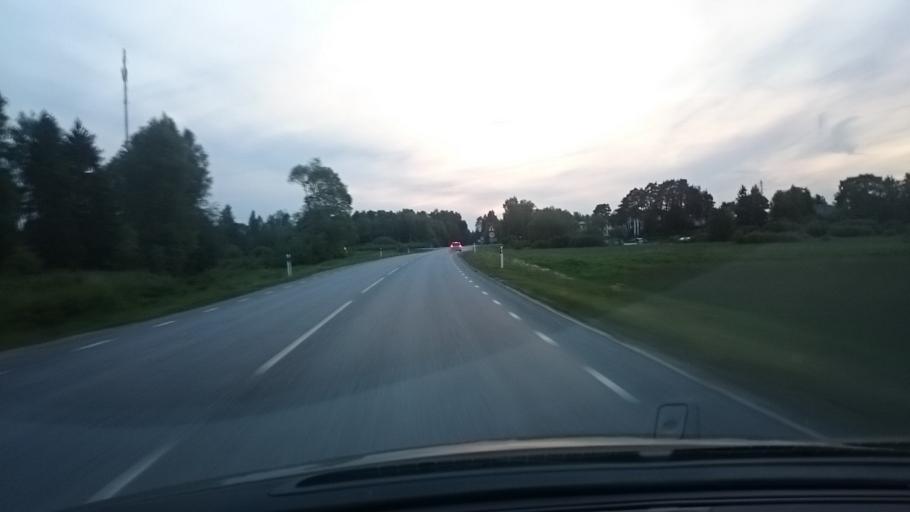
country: EE
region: Raplamaa
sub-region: Kehtna vald
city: Kehtna
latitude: 58.8575
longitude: 25.0016
